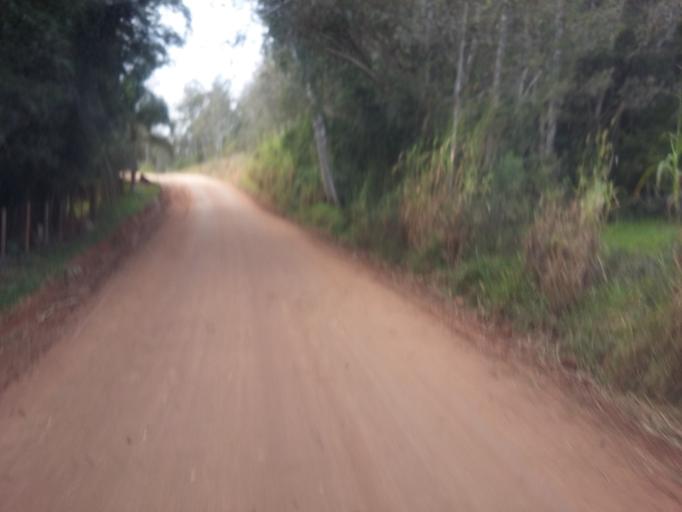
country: BR
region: Rio Grande do Sul
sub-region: Camaqua
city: Camaqua
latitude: -30.7167
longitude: -51.7857
